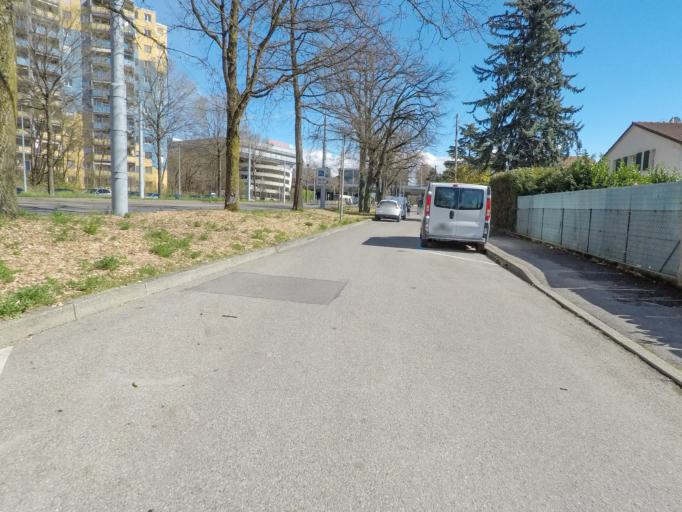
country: CH
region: Geneva
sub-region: Geneva
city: Les Avanchets
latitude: 46.2188
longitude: 6.1084
